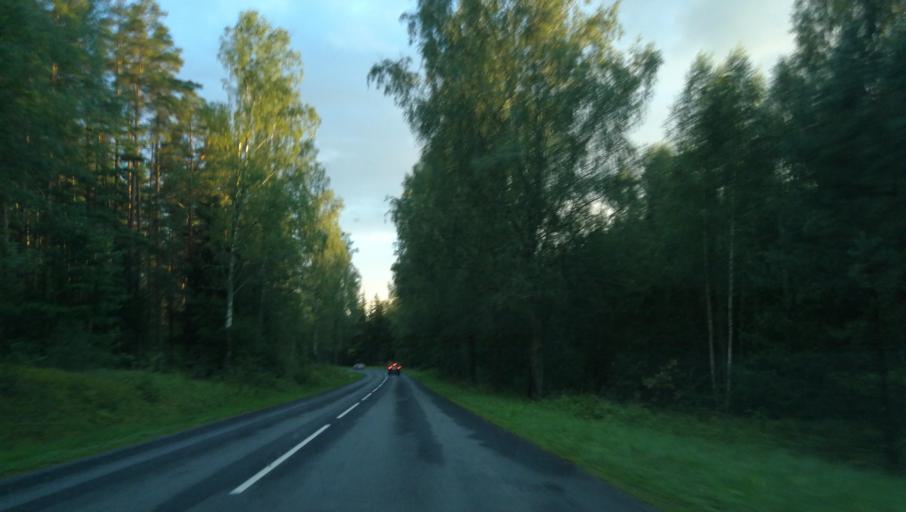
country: LV
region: Priekuli
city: Priekuli
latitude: 57.3686
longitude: 25.3833
